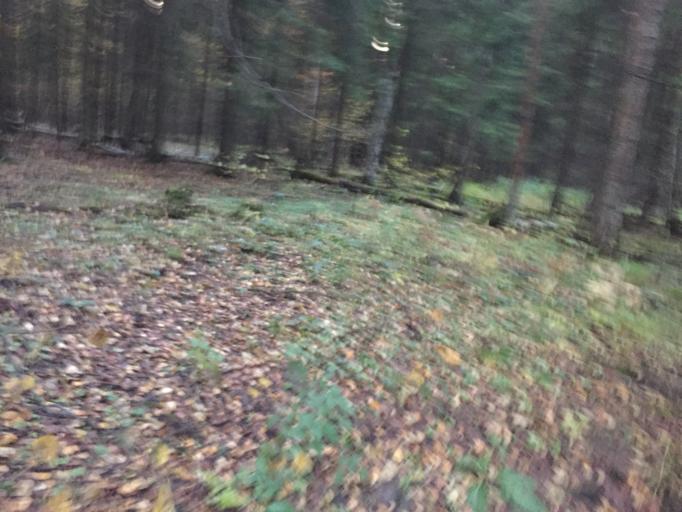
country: RU
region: Moskovskaya
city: Druzhba
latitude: 55.8612
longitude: 37.7806
